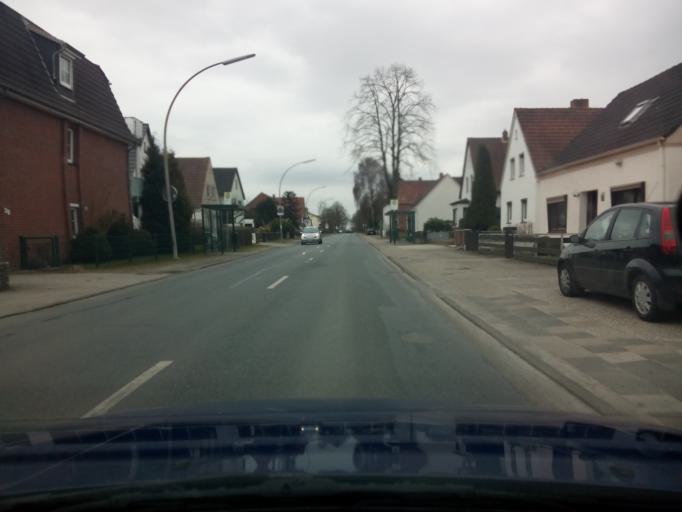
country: DE
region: Lower Saxony
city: Osterholz-Scharmbeck
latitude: 53.2326
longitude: 8.8087
